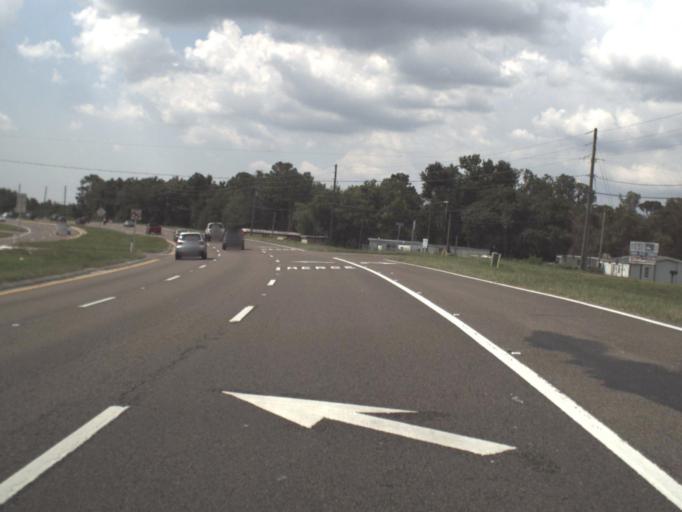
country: US
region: Florida
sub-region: Pasco County
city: Land O' Lakes
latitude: 28.2464
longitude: -82.4612
